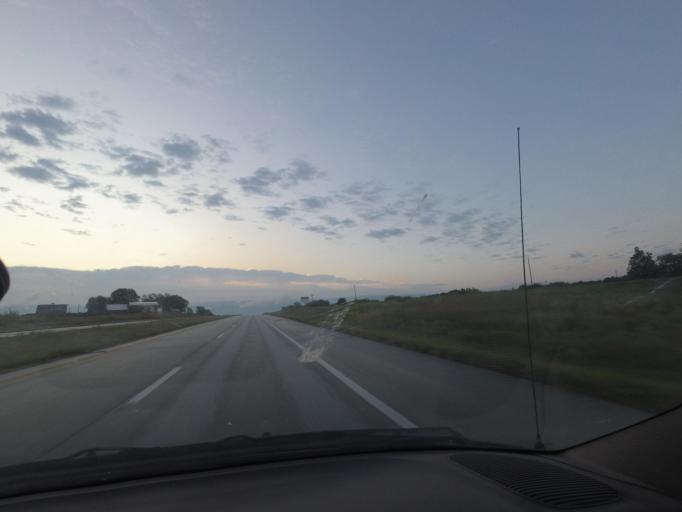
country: US
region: Missouri
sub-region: Macon County
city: Macon
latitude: 39.7541
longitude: -92.5372
